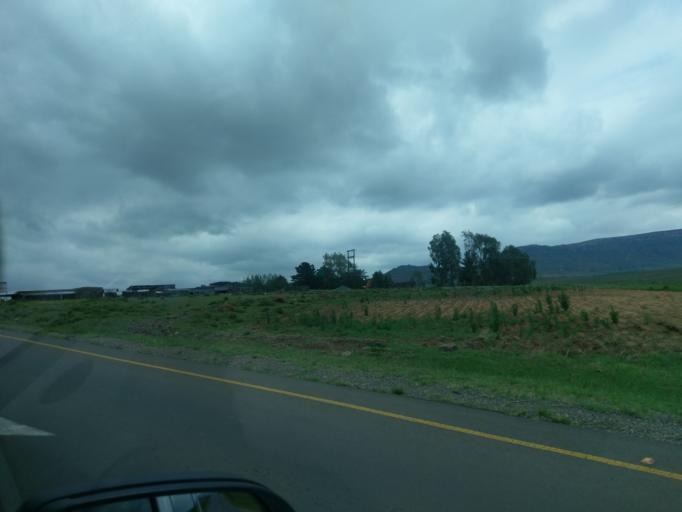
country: LS
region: Mafeteng
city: Mafeteng
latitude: -29.7092
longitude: 27.4250
